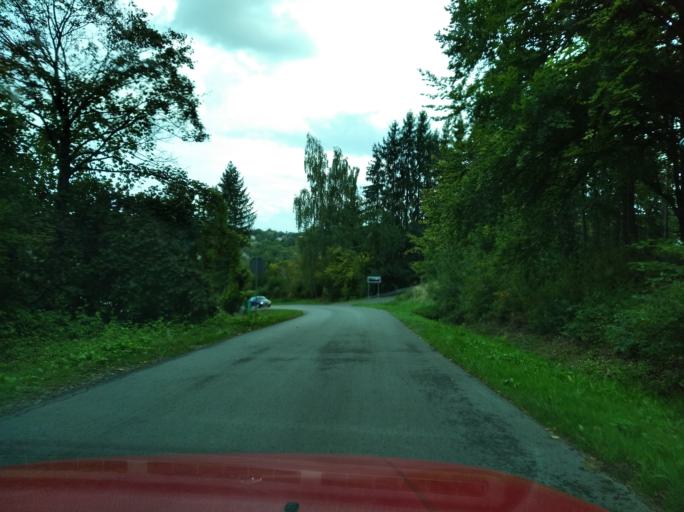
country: PL
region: Subcarpathian Voivodeship
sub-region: Powiat rzeszowski
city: Tyczyn
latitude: 49.9323
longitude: 22.0149
